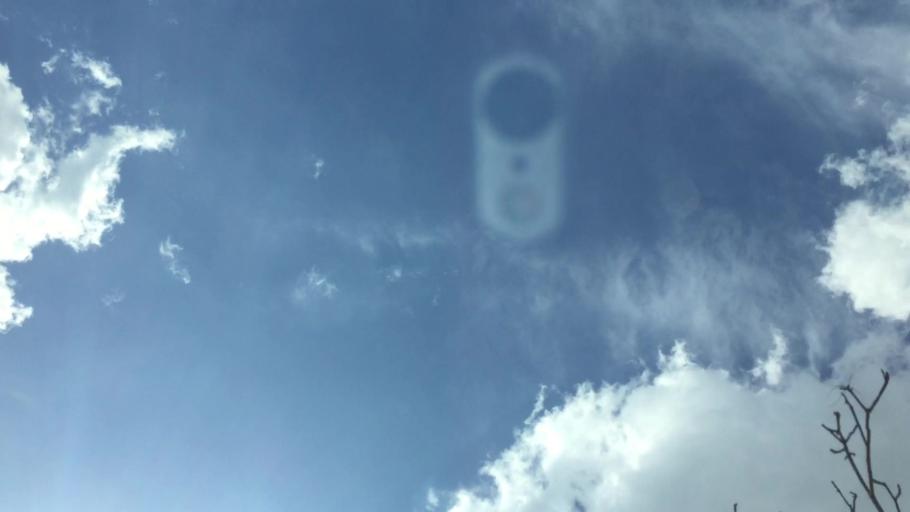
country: US
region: Texas
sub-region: Harris County
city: Bunker Hill Village
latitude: 29.7539
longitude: -95.5866
